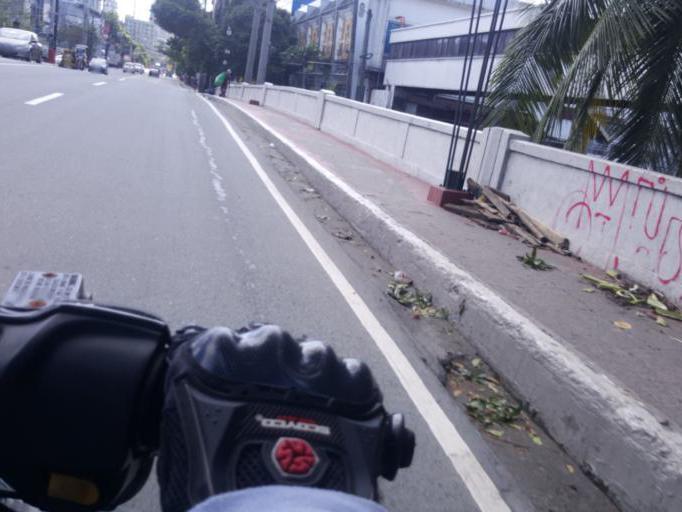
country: PH
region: Metro Manila
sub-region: City of Manila
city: Quiapo
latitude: 14.5851
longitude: 120.9928
